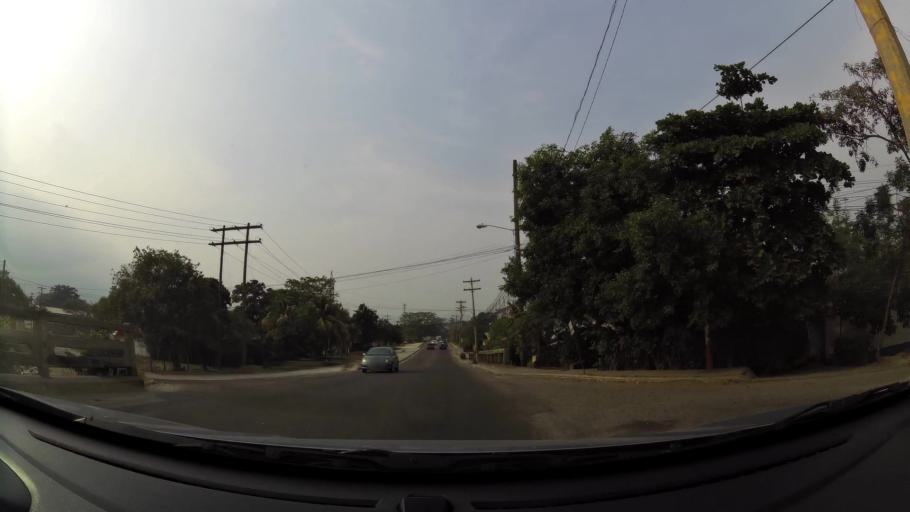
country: HN
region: Cortes
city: San Pedro Sula
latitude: 15.5326
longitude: -88.0140
